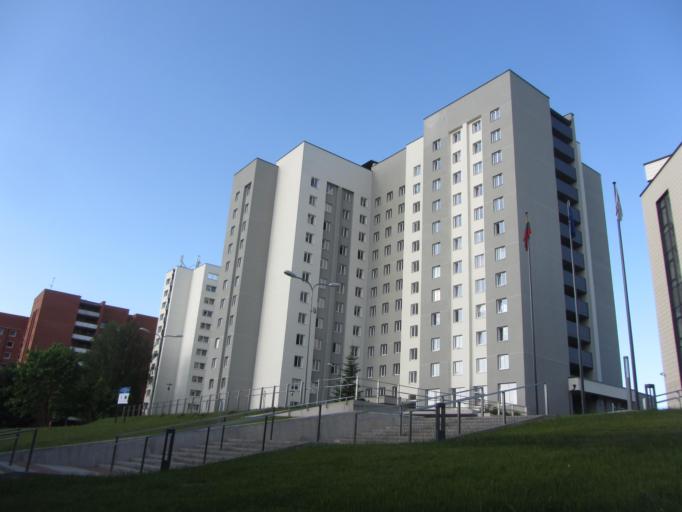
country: LT
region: Vilnius County
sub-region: Vilnius
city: Fabijoniskes
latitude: 54.7304
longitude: 25.2613
